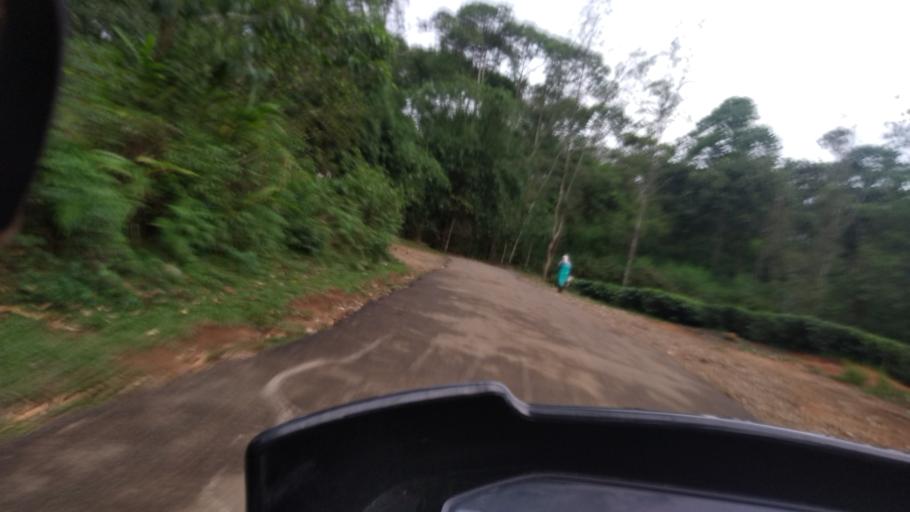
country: IN
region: Tamil Nadu
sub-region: Theni
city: Gudalur
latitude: 9.5464
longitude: 77.0525
